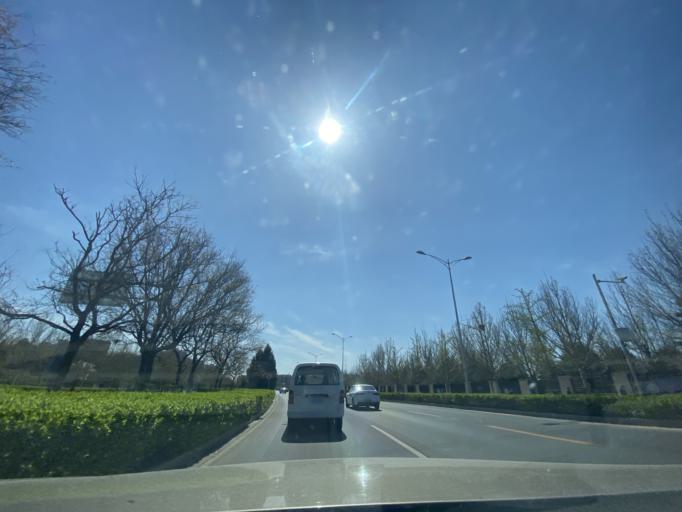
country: CN
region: Beijing
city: Sijiqing
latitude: 39.9377
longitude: 116.2406
